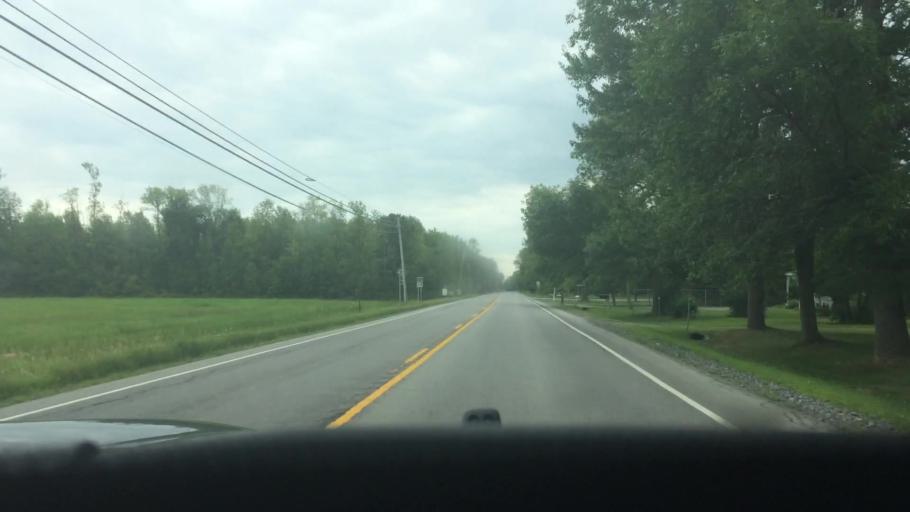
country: US
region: New York
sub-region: St. Lawrence County
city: Ogdensburg
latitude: 44.6538
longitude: -75.4463
